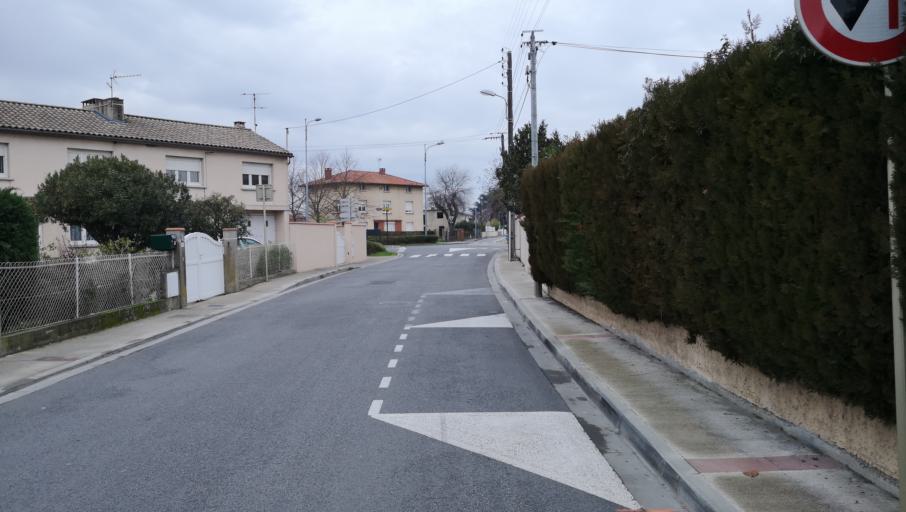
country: FR
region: Midi-Pyrenees
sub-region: Departement de la Haute-Garonne
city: Blagnac
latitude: 43.6414
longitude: 1.3849
